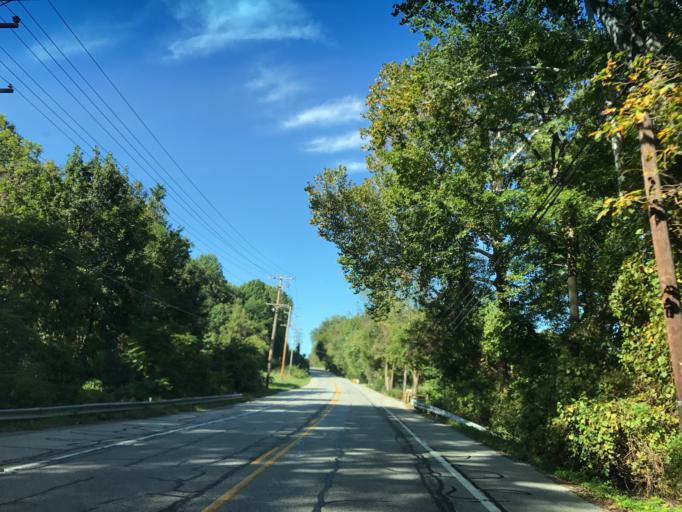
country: US
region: Maryland
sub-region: Anne Arundel County
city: Davidsonville
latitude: 38.9156
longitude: -76.6497
